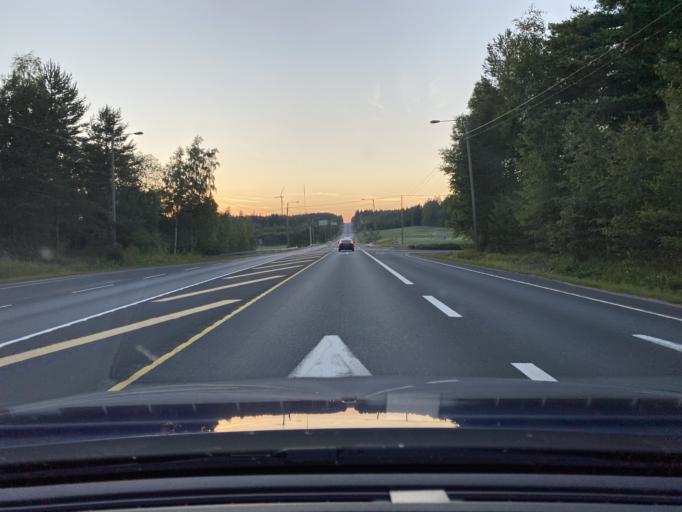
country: FI
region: Pirkanmaa
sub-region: Luoteis-Pirkanmaa
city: Ikaalinen
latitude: 61.7733
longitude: 23.0102
